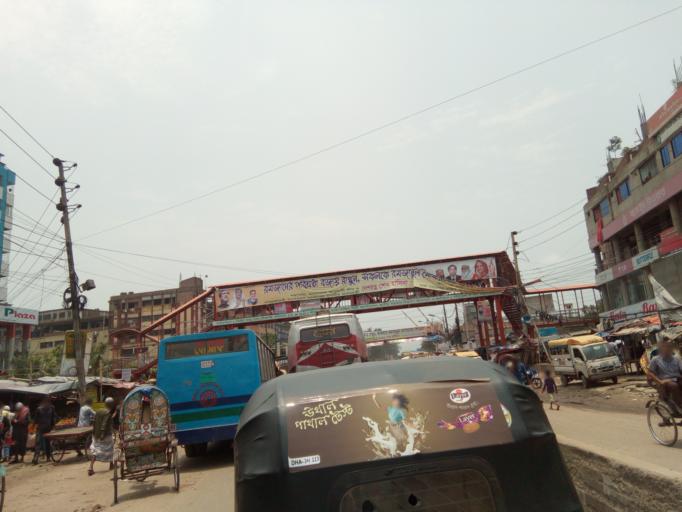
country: BD
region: Dhaka
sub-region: Dhaka
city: Dhaka
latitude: 23.6940
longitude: 90.4350
